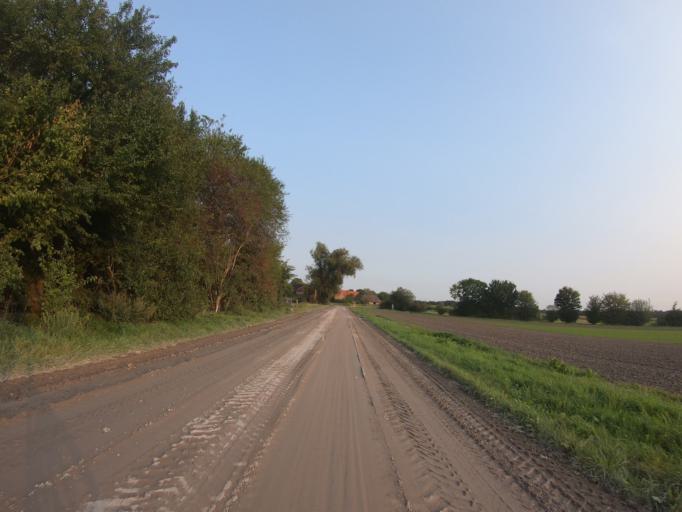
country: DE
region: Lower Saxony
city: Ribbesbuttel
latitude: 52.4261
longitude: 10.4792
